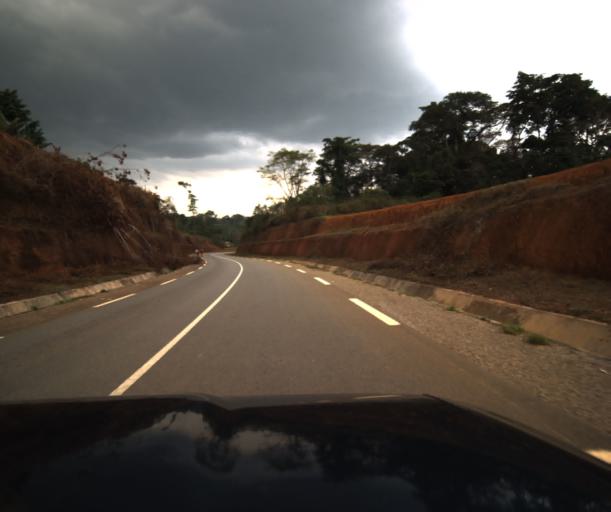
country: CM
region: Centre
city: Mbankomo
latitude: 3.6681
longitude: 11.3455
